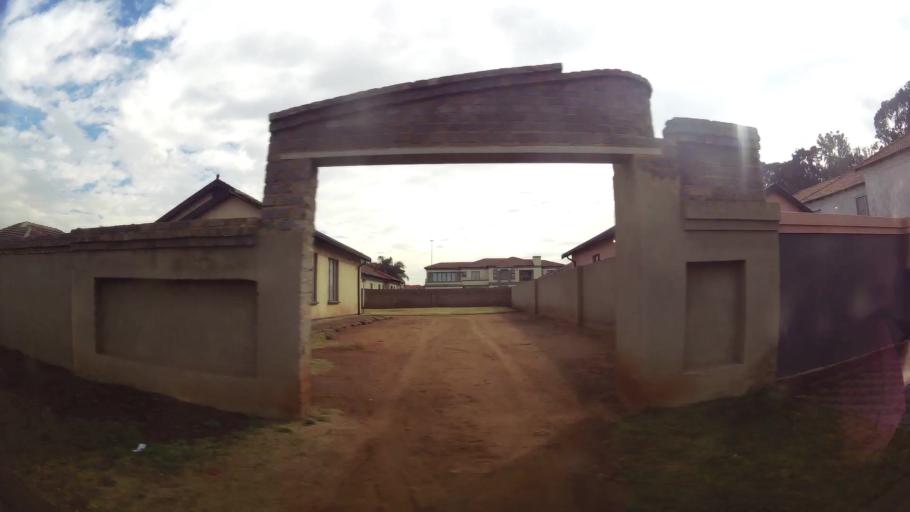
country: ZA
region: Gauteng
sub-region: Ekurhuleni Metropolitan Municipality
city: Germiston
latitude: -26.3279
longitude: 28.1888
